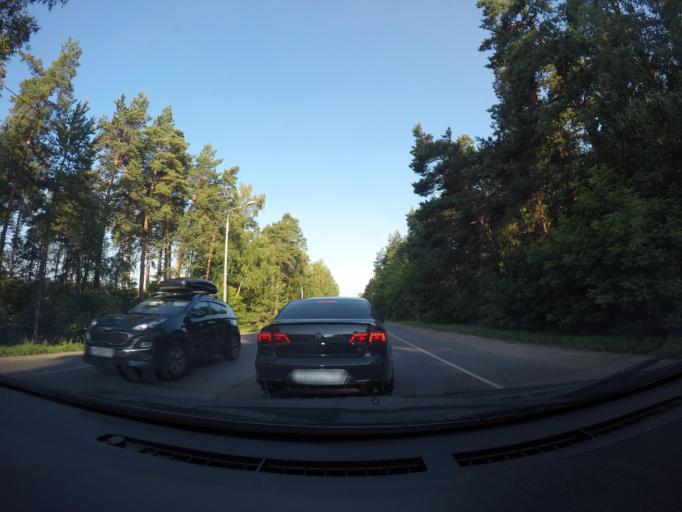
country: RU
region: Moskovskaya
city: Malakhovka
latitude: 55.6572
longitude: 38.0443
